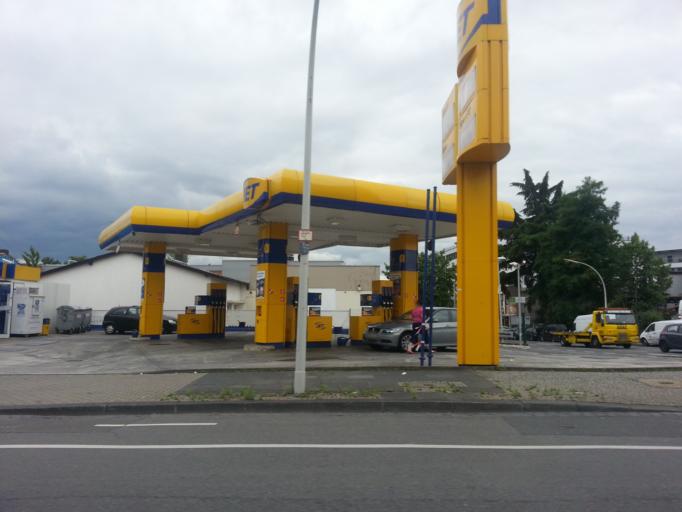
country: DE
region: North Rhine-Westphalia
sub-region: Regierungsbezirk Koln
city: Bonn
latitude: 50.7401
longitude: 7.0761
